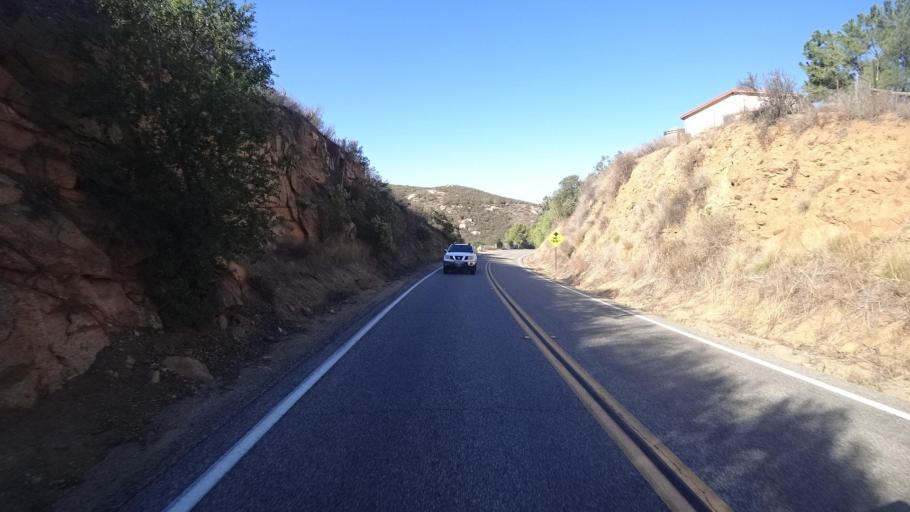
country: US
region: California
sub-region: San Diego County
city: Jamul
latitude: 32.6725
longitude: -116.7749
